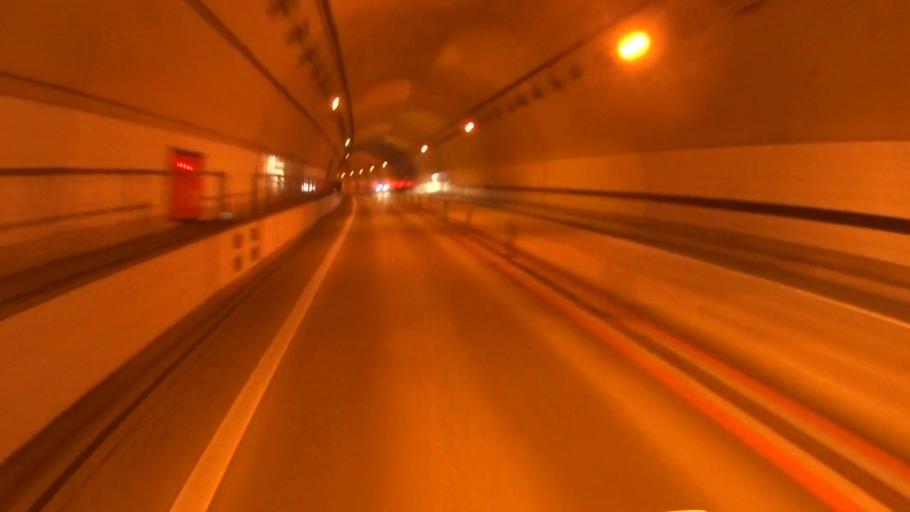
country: JP
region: Kyoto
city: Miyazu
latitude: 35.4914
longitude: 135.1721
